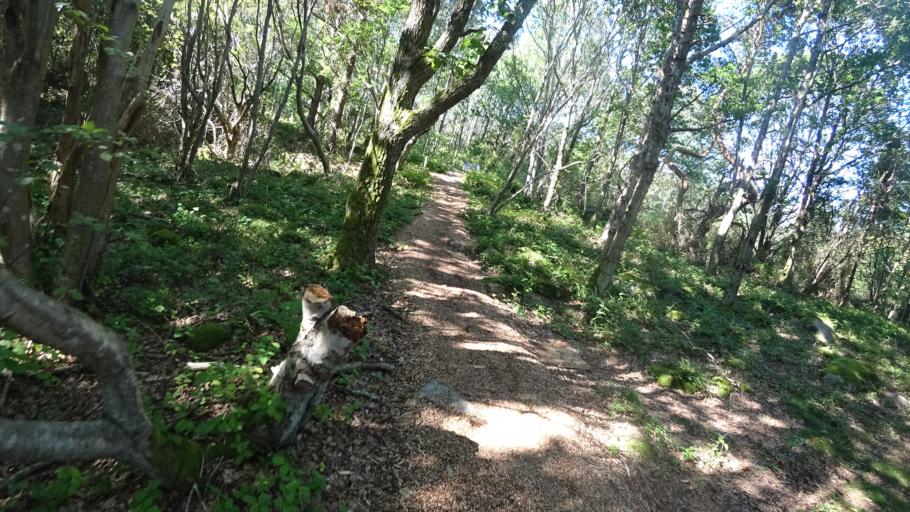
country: SE
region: Vaestra Goetaland
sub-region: Goteborg
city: Styrso
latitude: 57.6075
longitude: 11.7850
